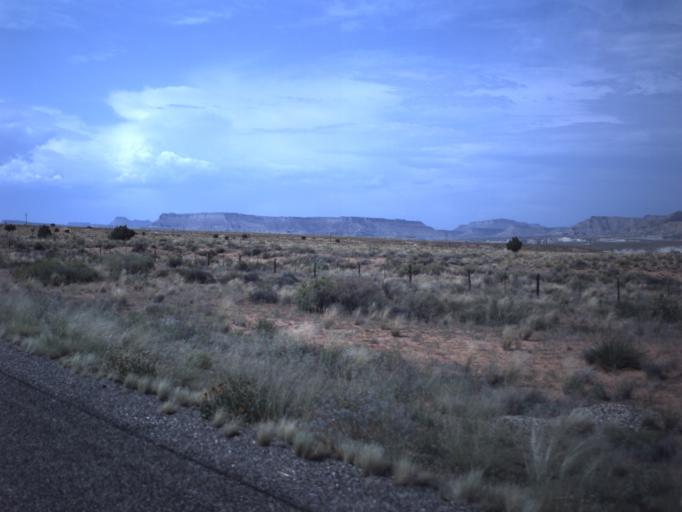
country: US
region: Arizona
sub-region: Coconino County
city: Page
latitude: 37.0818
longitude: -111.6730
